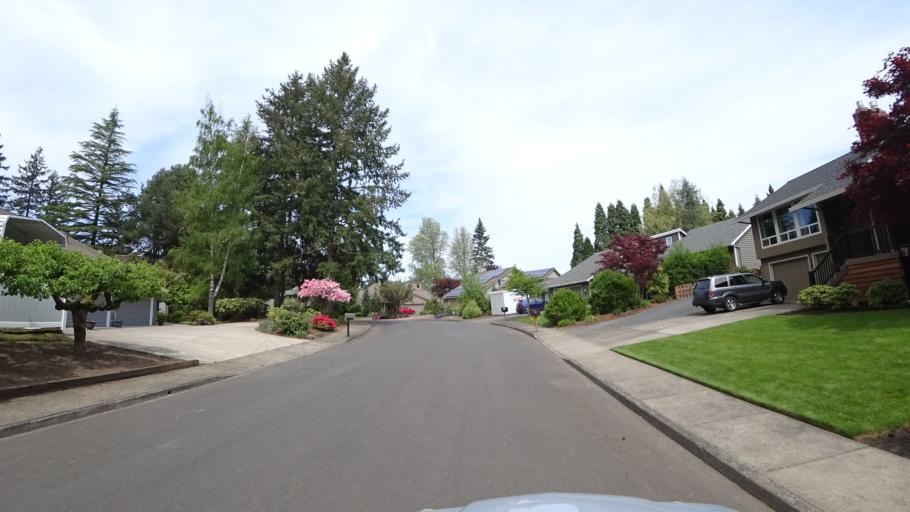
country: US
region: Oregon
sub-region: Washington County
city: Hillsboro
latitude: 45.5133
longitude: -122.9425
